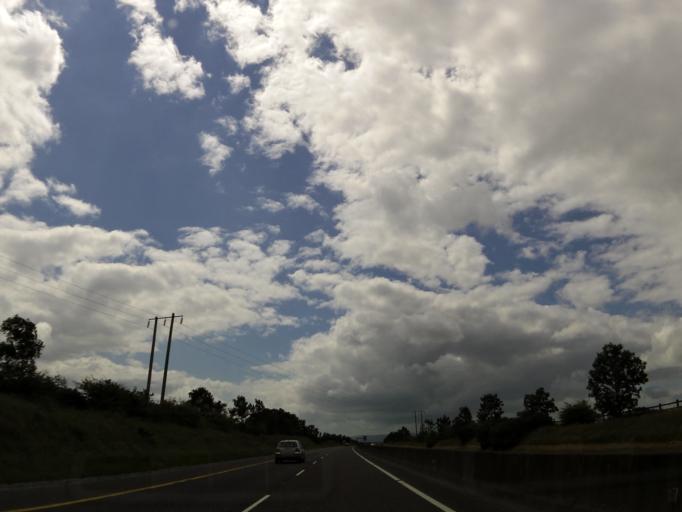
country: IE
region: Munster
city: Cashel
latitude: 52.5177
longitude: -7.8616
